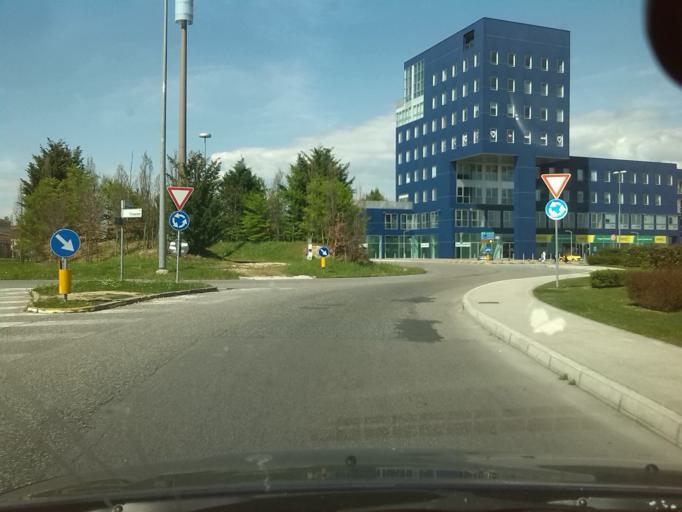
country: IT
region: Friuli Venezia Giulia
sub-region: Provincia di Udine
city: Feletto Umberto
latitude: 46.0943
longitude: 13.2314
